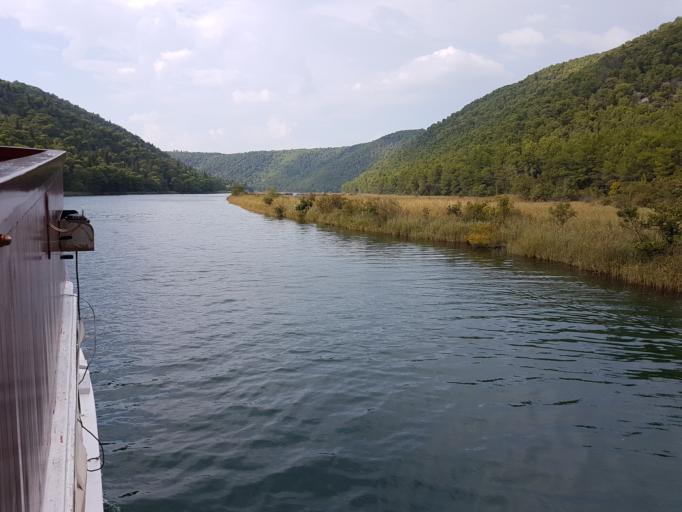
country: HR
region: Sibensko-Kniniska
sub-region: Grad Sibenik
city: Sibenik
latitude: 43.8100
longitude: 15.9570
